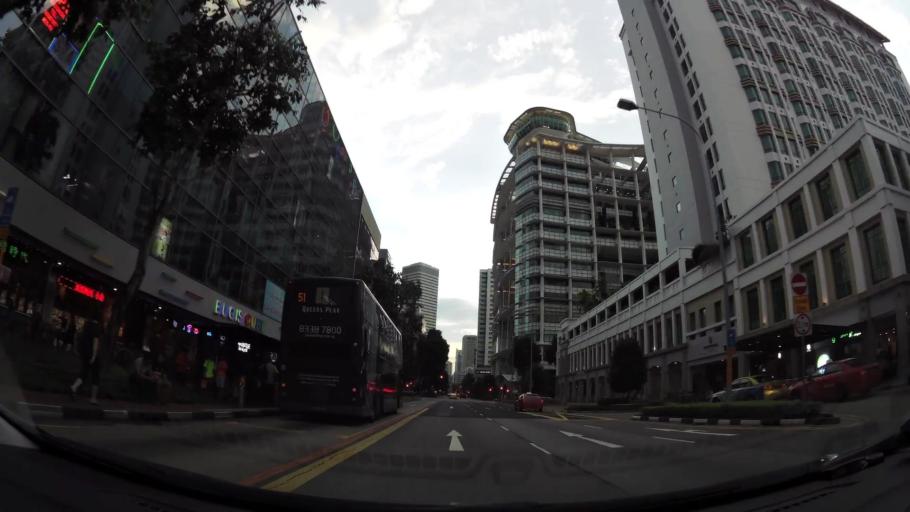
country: SG
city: Singapore
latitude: 1.2985
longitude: 103.8557
